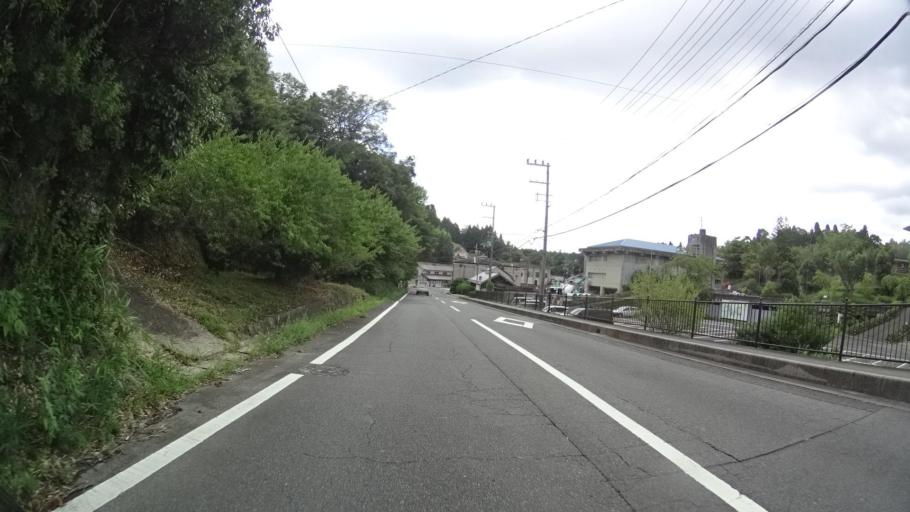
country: JP
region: Mie
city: Ueno-ebisumachi
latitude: 34.7102
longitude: 136.0451
